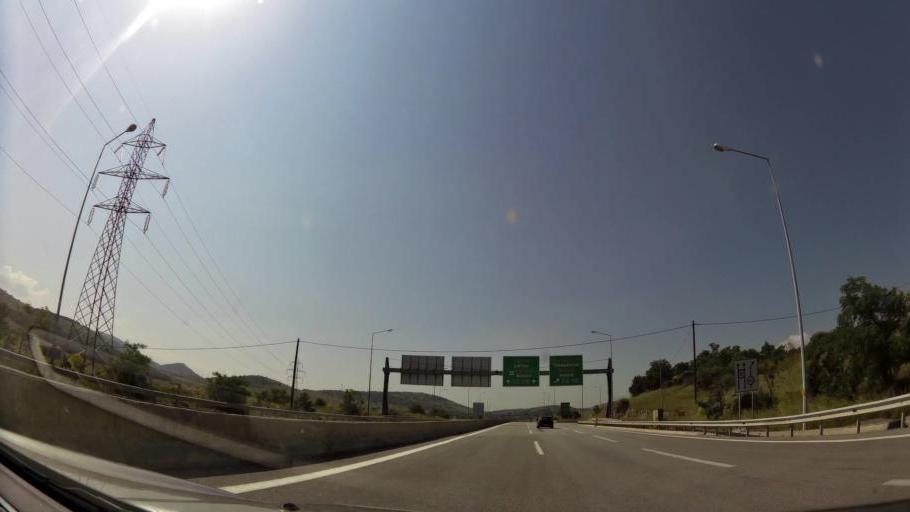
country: GR
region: West Macedonia
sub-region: Nomos Kozanis
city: Koila
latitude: 40.3481
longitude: 21.8052
